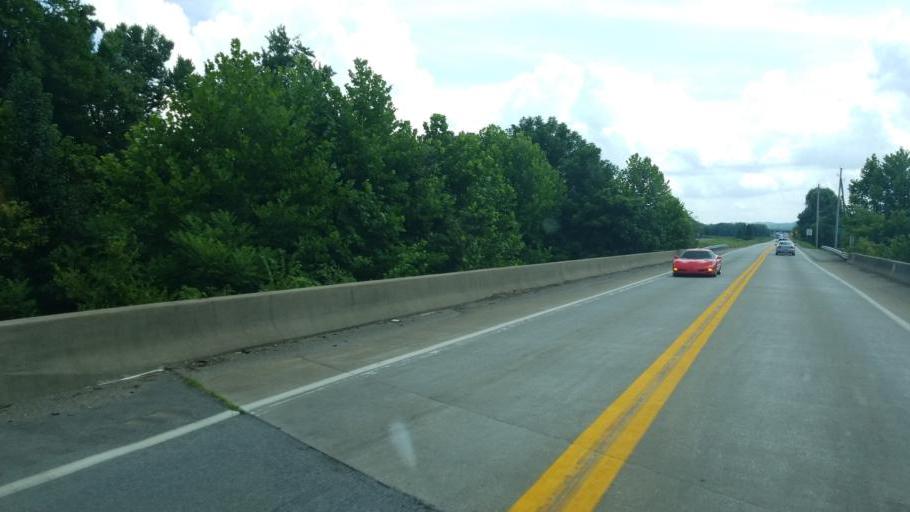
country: US
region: West Virginia
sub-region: Putnam County
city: Buffalo
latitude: 38.5920
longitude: -82.0059
